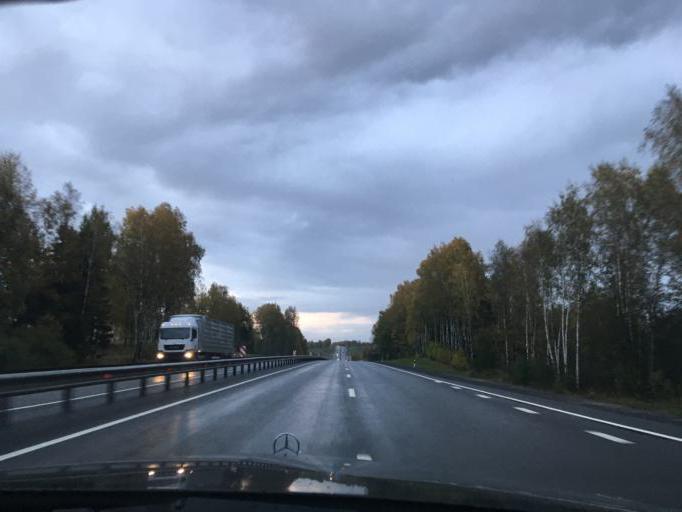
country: RU
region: Smolensk
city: Safonovo
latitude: 55.1680
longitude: 33.4121
